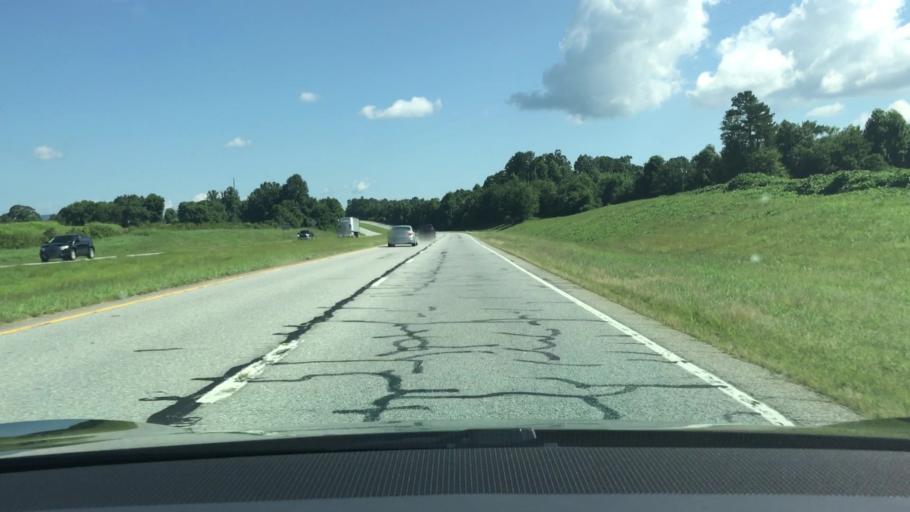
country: US
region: Georgia
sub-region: Habersham County
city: Clarkesville
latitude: 34.6171
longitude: -83.4478
